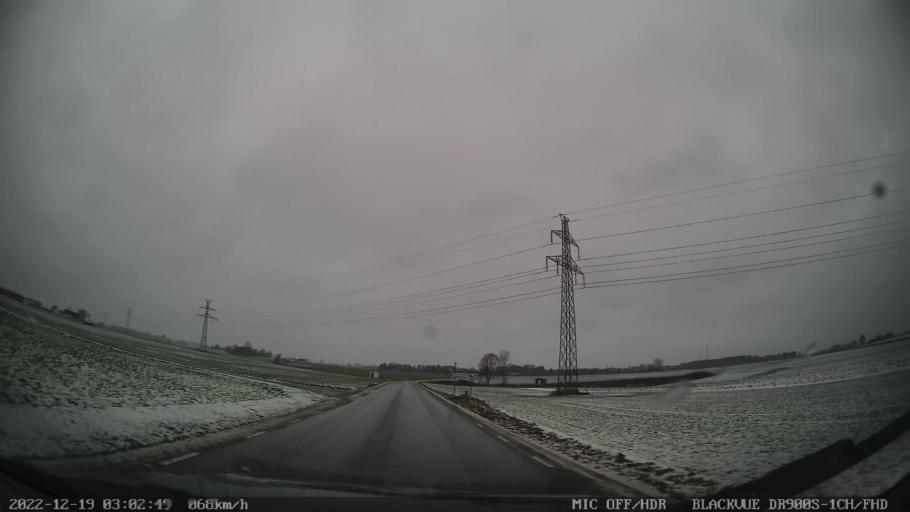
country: SE
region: Skane
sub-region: Tomelilla Kommun
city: Tomelilla
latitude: 55.5325
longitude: 14.0417
